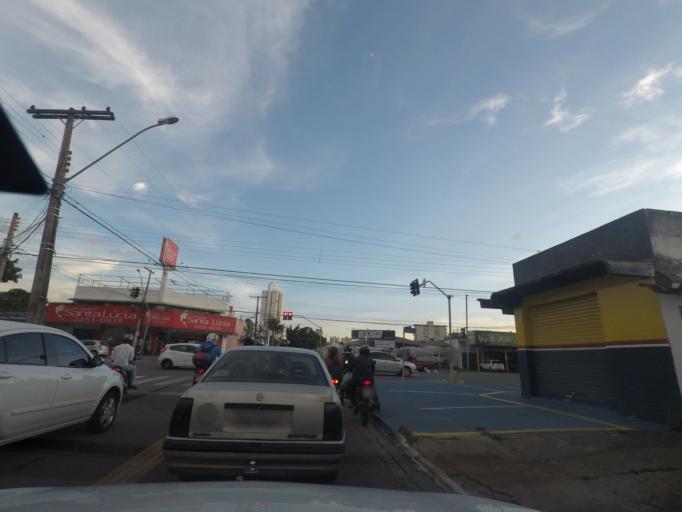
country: BR
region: Goias
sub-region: Goiania
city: Goiania
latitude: -16.6959
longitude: -49.2865
